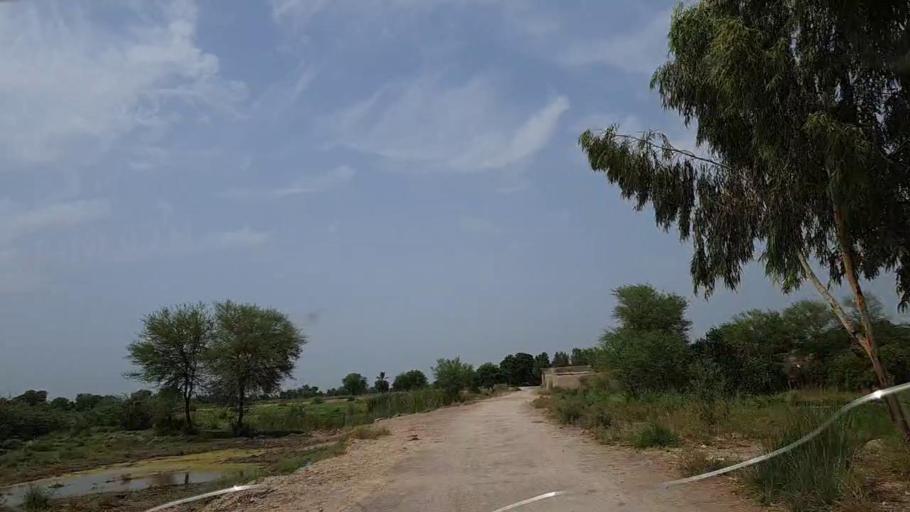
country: PK
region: Sindh
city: Tharu Shah
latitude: 26.9028
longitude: 68.0750
